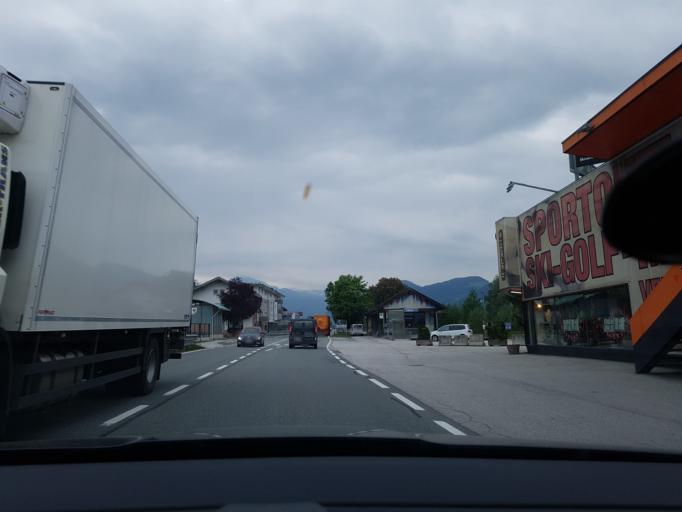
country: AT
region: Tyrol
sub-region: Politischer Bezirk Schwaz
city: Uderns
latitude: 47.3257
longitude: 11.8652
